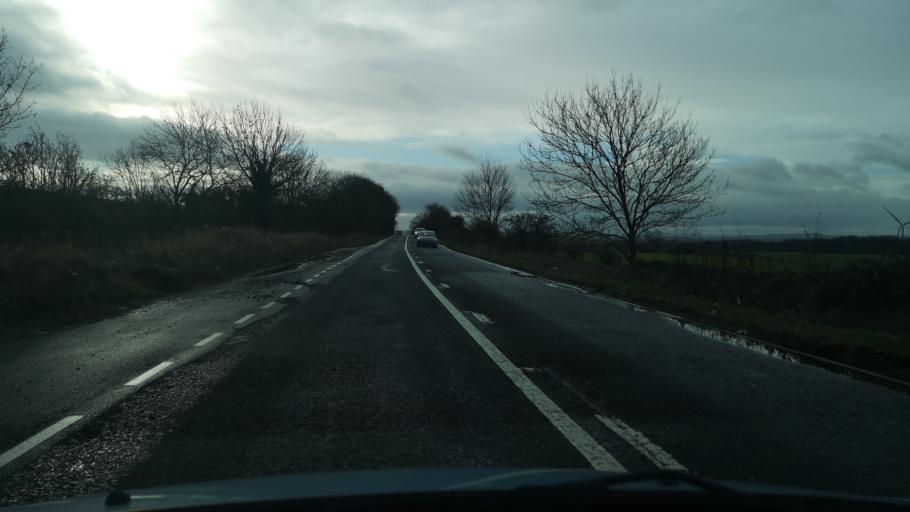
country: GB
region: England
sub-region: Barnsley
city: Great Houghton
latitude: 53.5646
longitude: -1.3504
